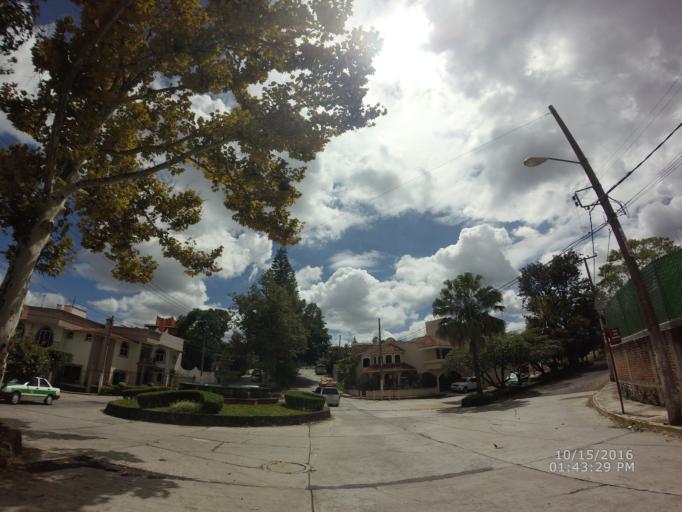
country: MX
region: Veracruz
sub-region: Xalapa
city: Lomas Verdes
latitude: 19.5298
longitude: -96.8871
